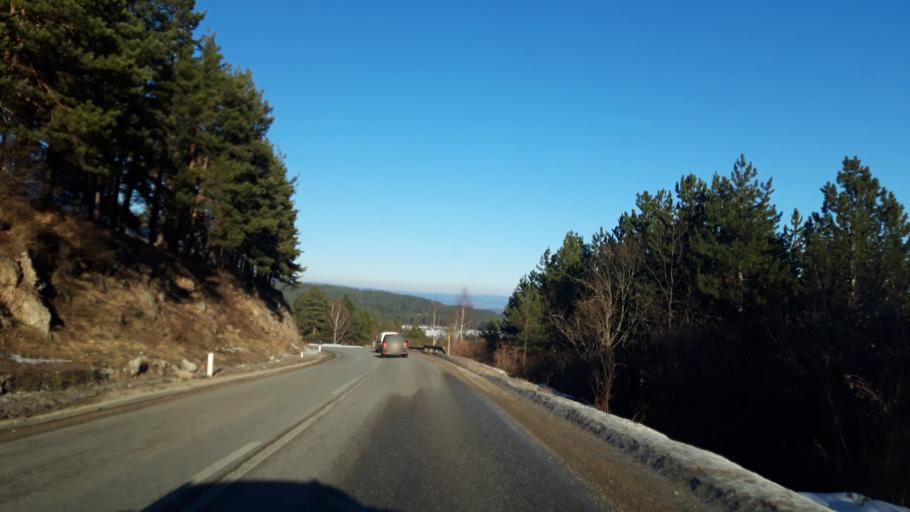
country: BA
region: Republika Srpska
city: Sokolac
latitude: 43.9108
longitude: 18.7176
